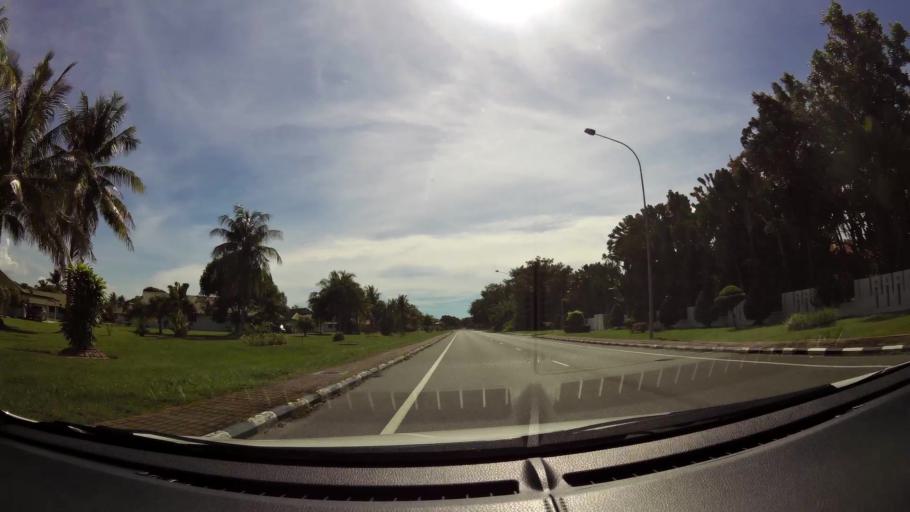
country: BN
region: Belait
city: Kuala Belait
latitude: 4.5884
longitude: 114.1981
